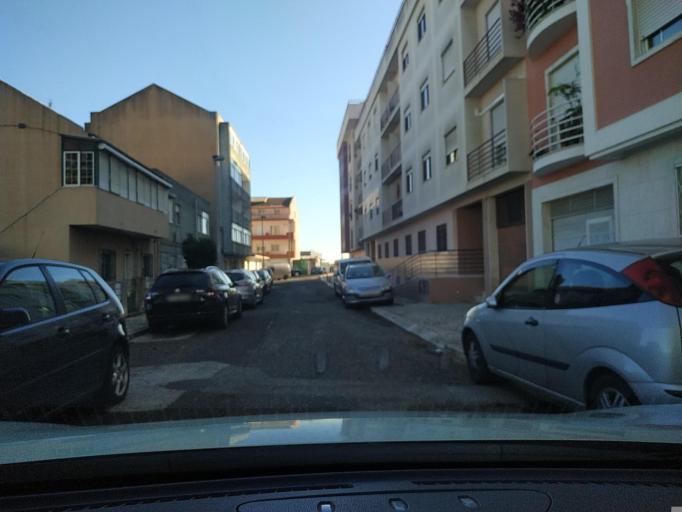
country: PT
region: Lisbon
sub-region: Odivelas
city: Pontinha
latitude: 38.7677
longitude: -9.2171
